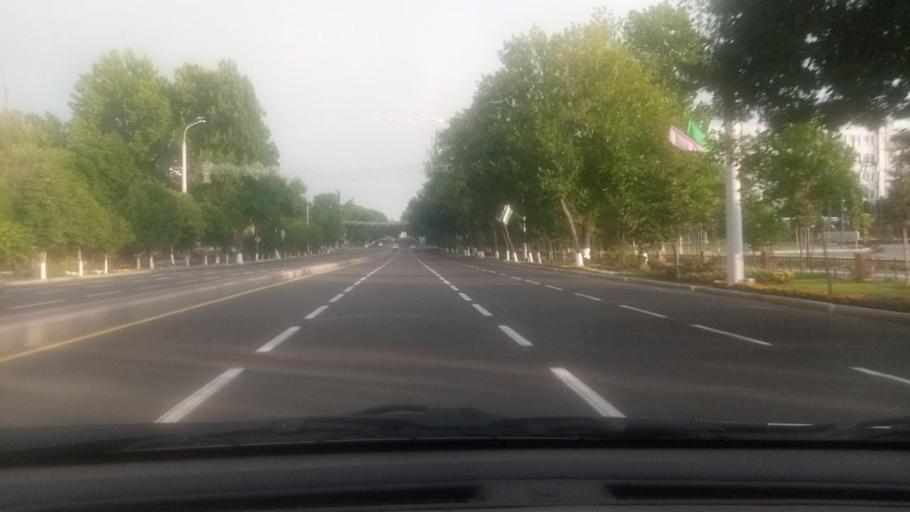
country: UZ
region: Toshkent
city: Salor
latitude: 41.3368
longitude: 69.3420
